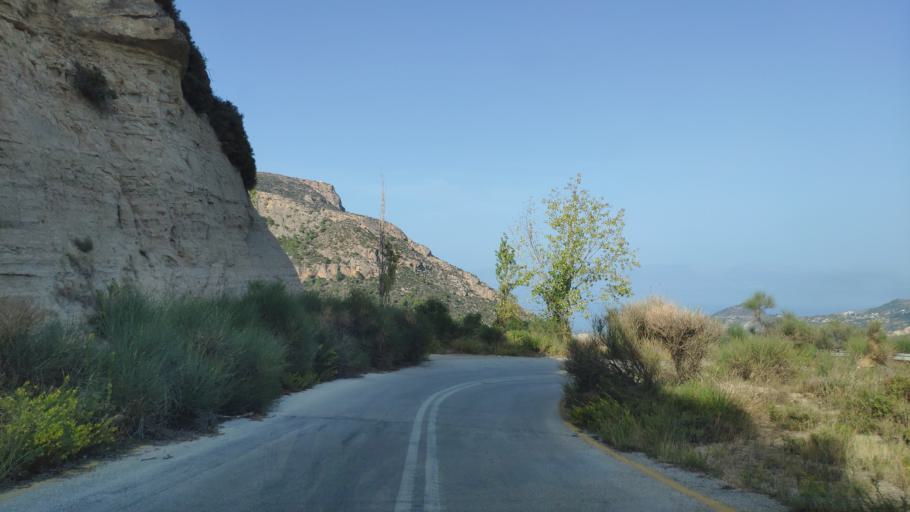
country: GR
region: West Greece
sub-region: Nomos Achaias
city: Aiyira
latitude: 38.0700
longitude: 22.3865
